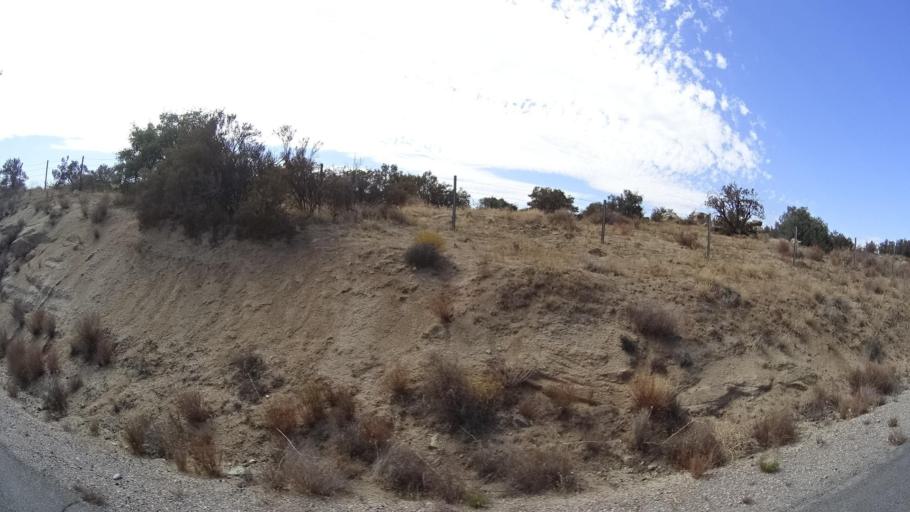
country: MX
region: Baja California
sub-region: Tecate
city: Cereso del Hongo
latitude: 32.6692
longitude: -116.2601
